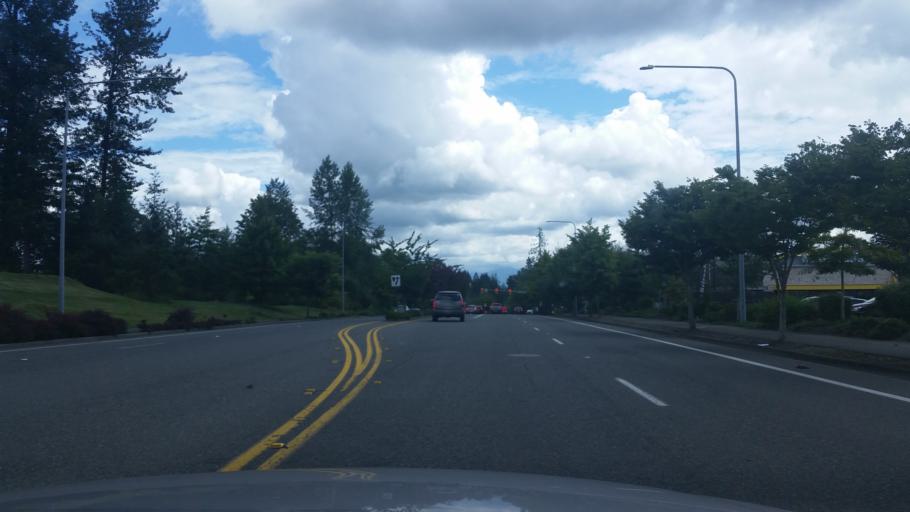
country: US
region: Washington
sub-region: King County
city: Union Hill-Novelty Hill
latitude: 47.6999
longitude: -122.0264
